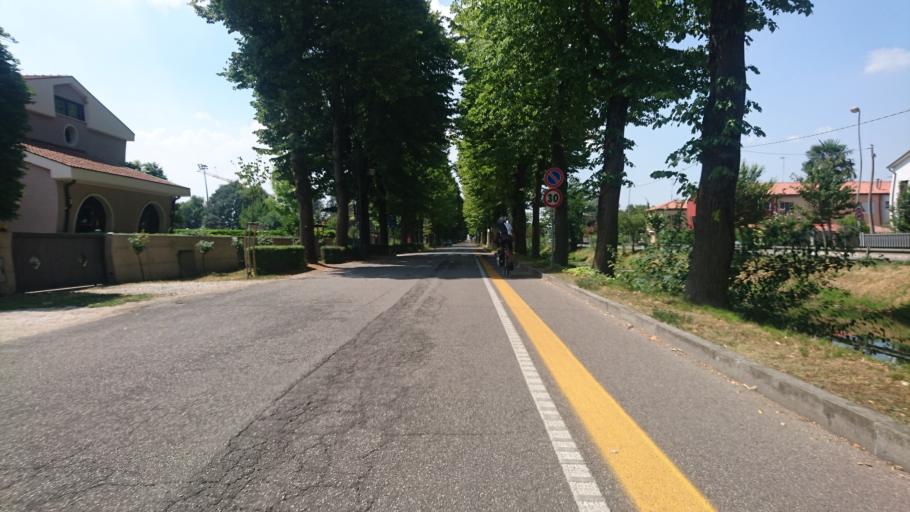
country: IT
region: Veneto
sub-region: Provincia di Padova
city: Piove di Sacco-Piovega
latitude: 45.2983
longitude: 12.0297
